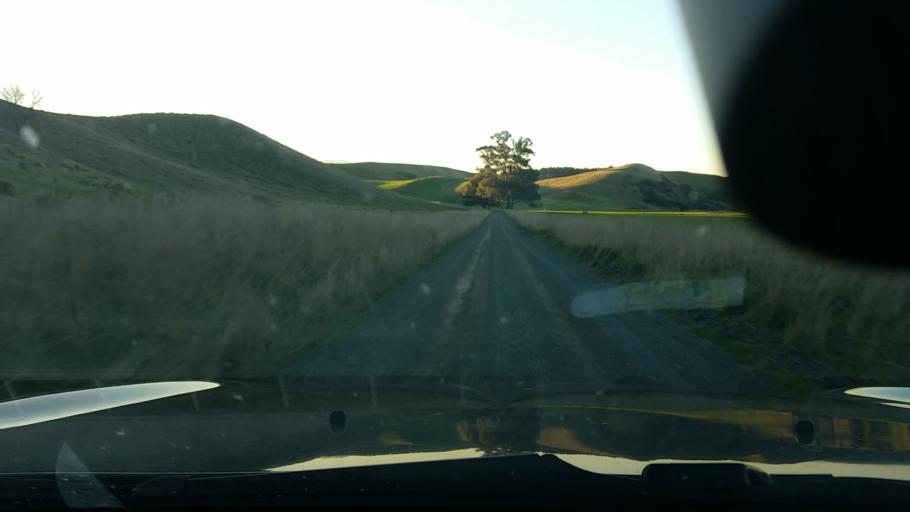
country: NZ
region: Marlborough
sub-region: Marlborough District
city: Blenheim
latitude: -41.7466
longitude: 174.0563
